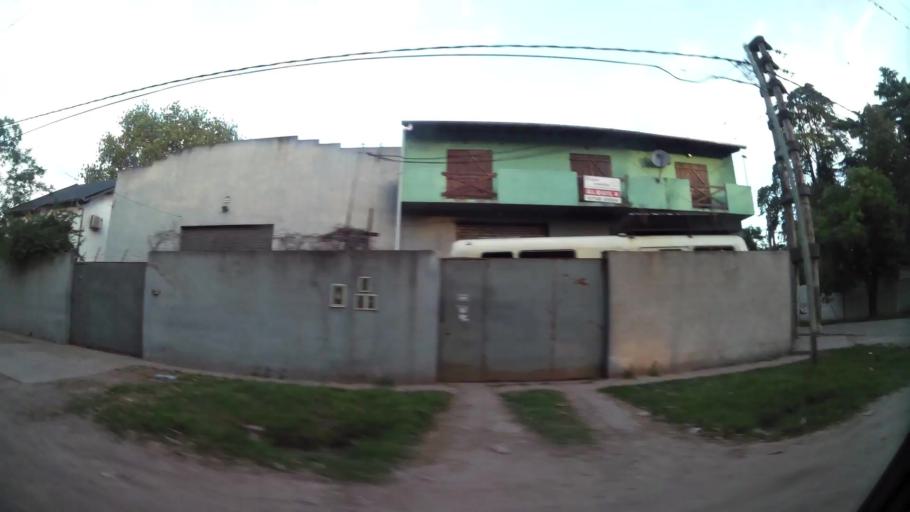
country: AR
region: Buenos Aires
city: Santa Catalina - Dique Lujan
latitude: -34.4518
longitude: -58.6634
